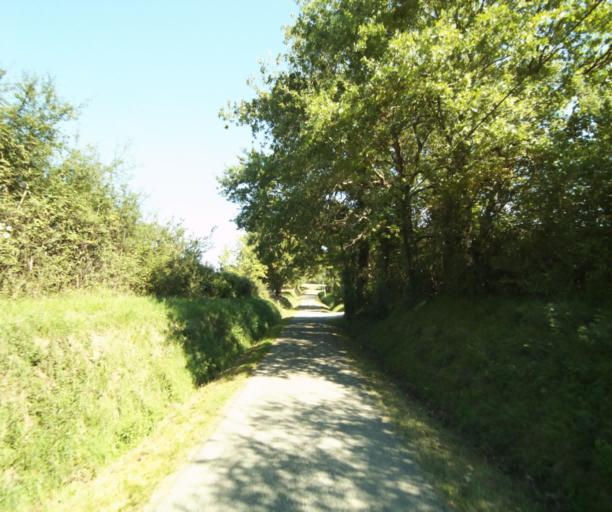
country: FR
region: Midi-Pyrenees
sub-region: Departement du Gers
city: Cazaubon
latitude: 43.9372
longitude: -0.0262
